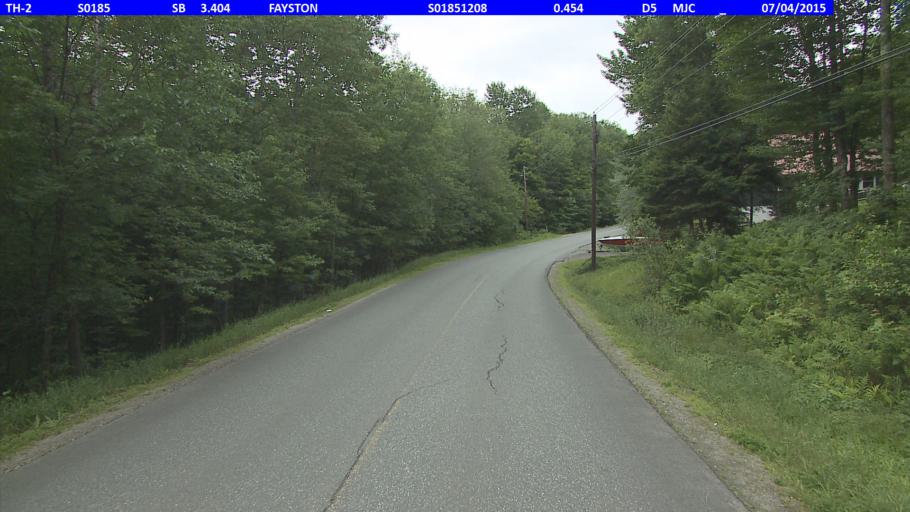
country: US
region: Vermont
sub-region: Addison County
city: Bristol
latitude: 44.1630
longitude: -72.8849
